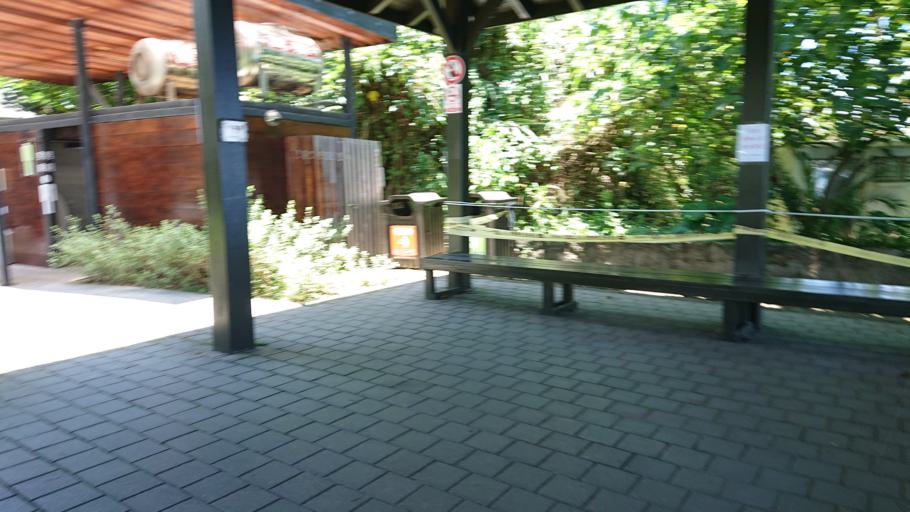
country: TW
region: Taiwan
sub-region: Hualien
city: Hualian
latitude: 23.7311
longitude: 121.5588
